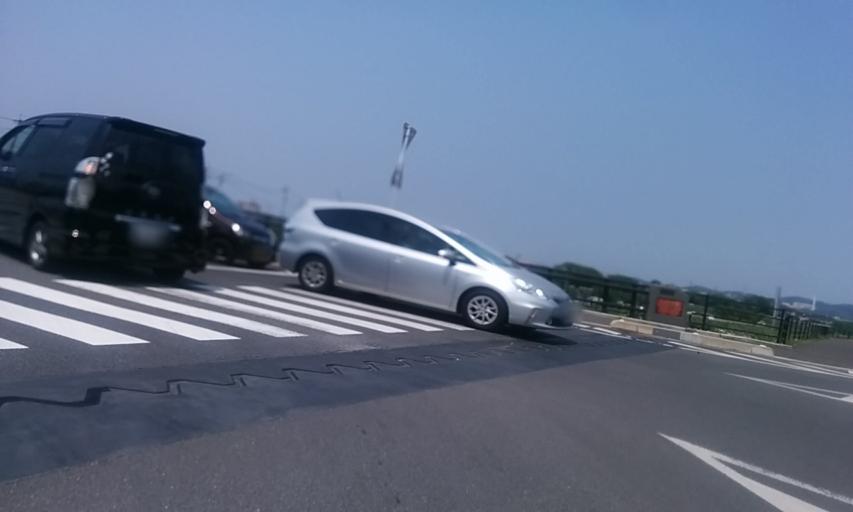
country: JP
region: Ehime
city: Niihama
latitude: 33.9233
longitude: 133.3092
